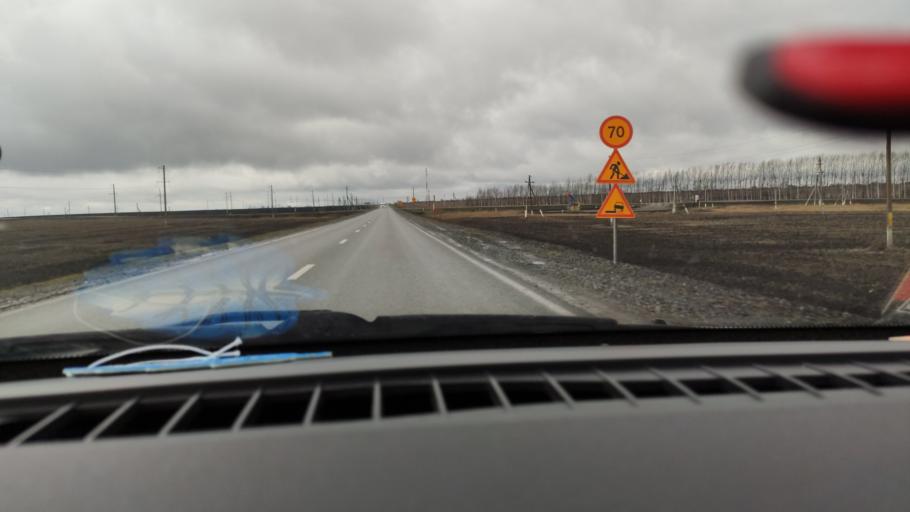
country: RU
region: Tatarstan
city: Nurlat
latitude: 54.4574
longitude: 50.8298
